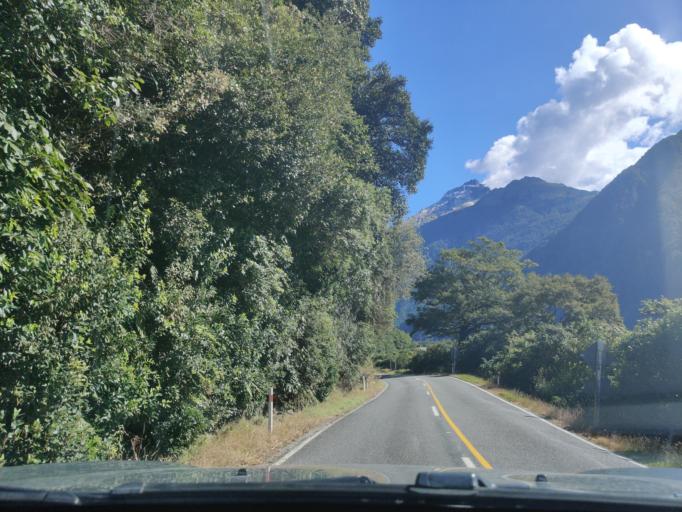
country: NZ
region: Otago
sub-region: Queenstown-Lakes District
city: Wanaka
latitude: -43.9748
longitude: 169.4235
